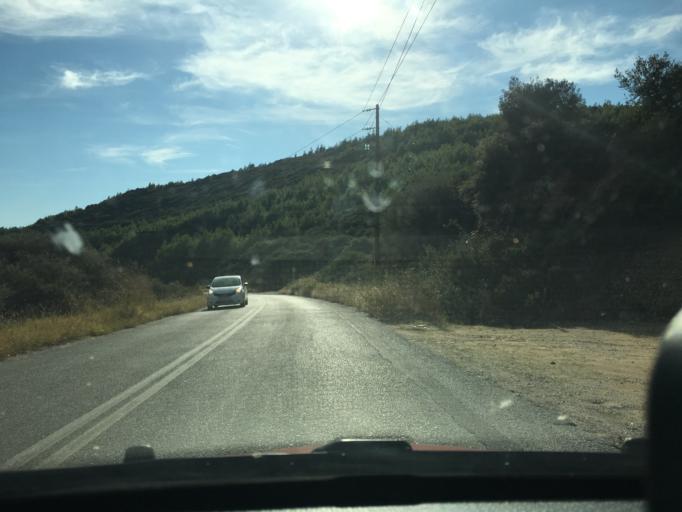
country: GR
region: Central Macedonia
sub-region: Nomos Chalkidikis
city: Agios Nikolaos
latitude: 40.3216
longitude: 23.6985
